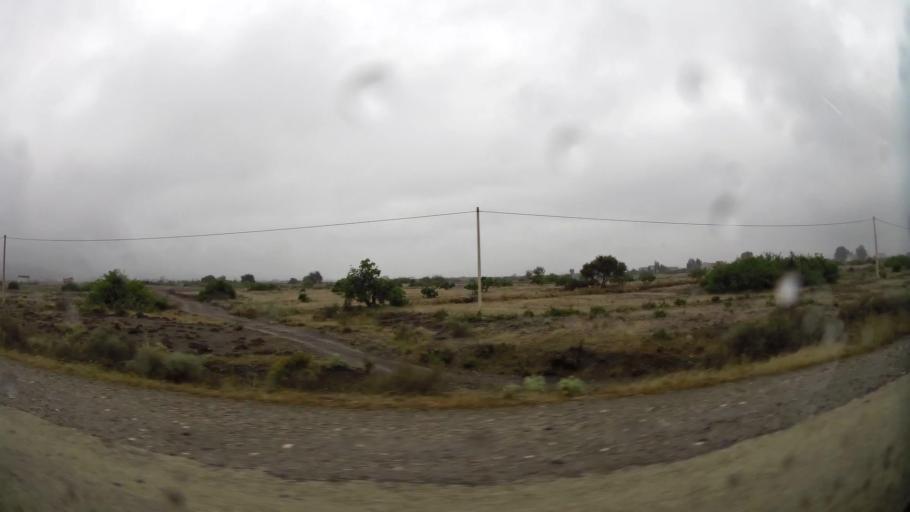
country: MA
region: Taza-Al Hoceima-Taounate
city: Imzourene
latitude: 35.1413
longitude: -3.7928
